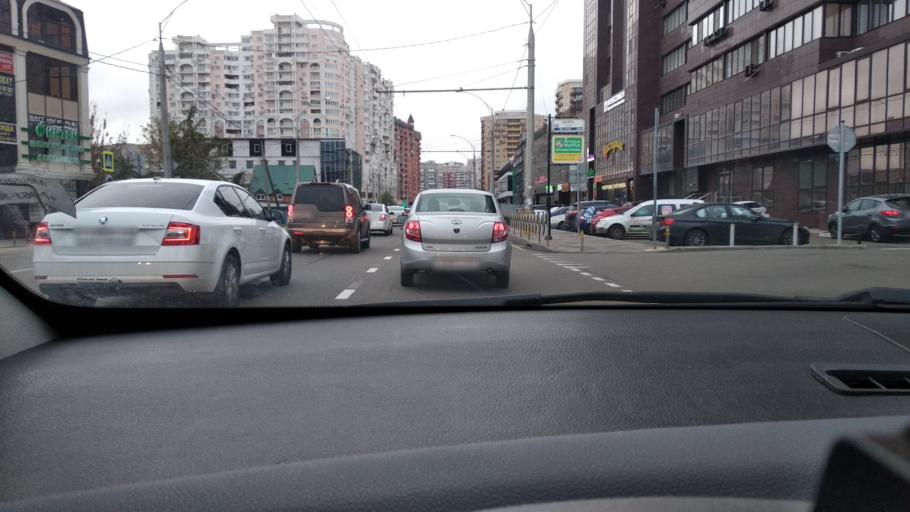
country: RU
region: Krasnodarskiy
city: Krasnodar
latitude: 45.0241
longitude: 38.9596
